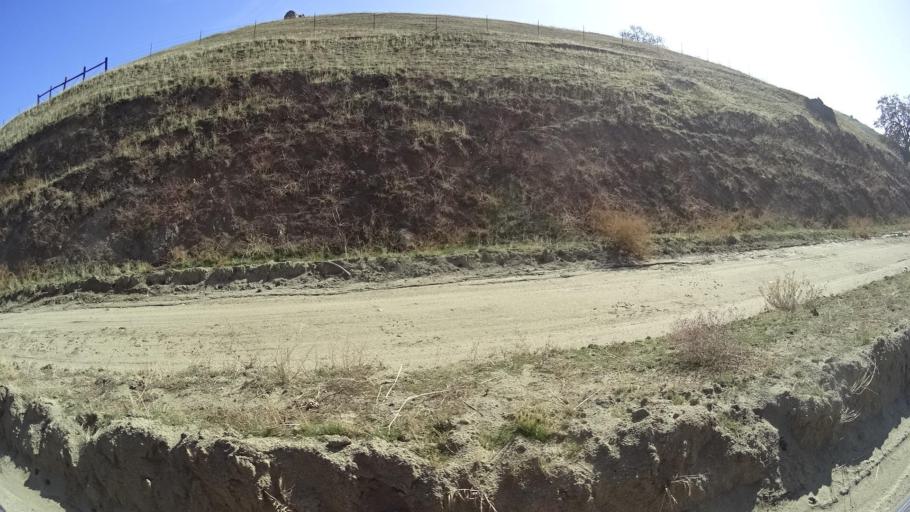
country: US
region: California
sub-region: Kern County
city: Oildale
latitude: 35.4864
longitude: -118.8146
